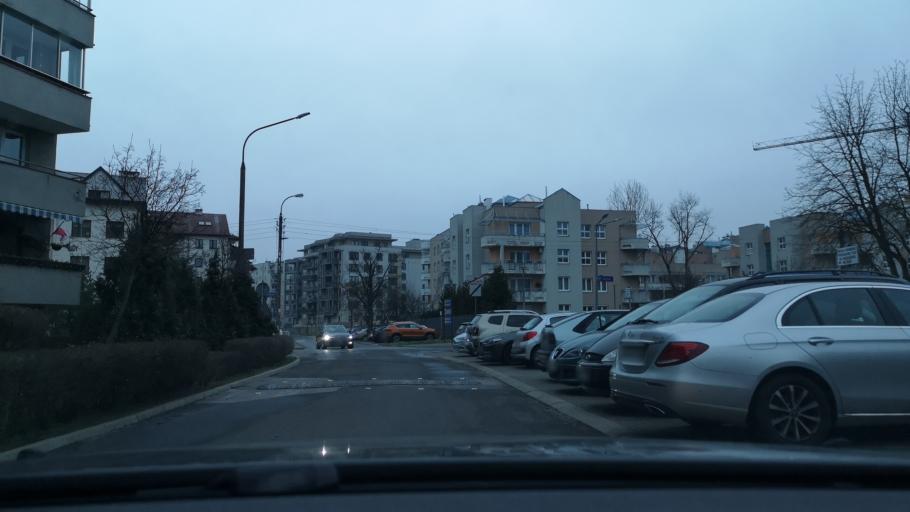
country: PL
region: Masovian Voivodeship
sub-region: Warszawa
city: Bemowo
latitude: 52.2439
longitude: 20.9204
